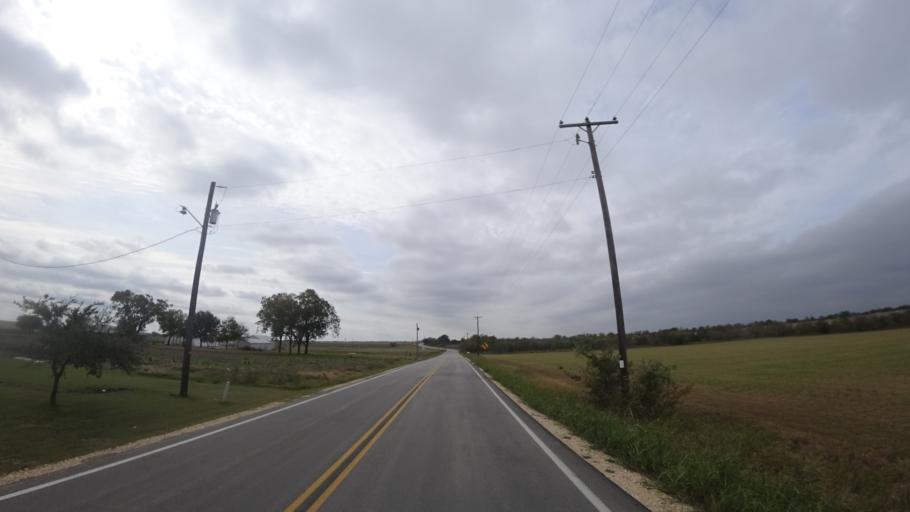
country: US
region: Texas
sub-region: Travis County
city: Manor
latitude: 30.3915
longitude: -97.5514
